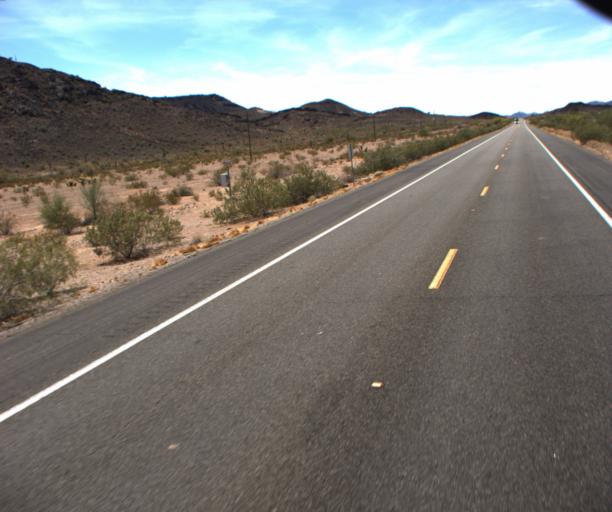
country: US
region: Arizona
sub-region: La Paz County
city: Quartzsite
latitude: 33.6870
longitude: -113.9157
